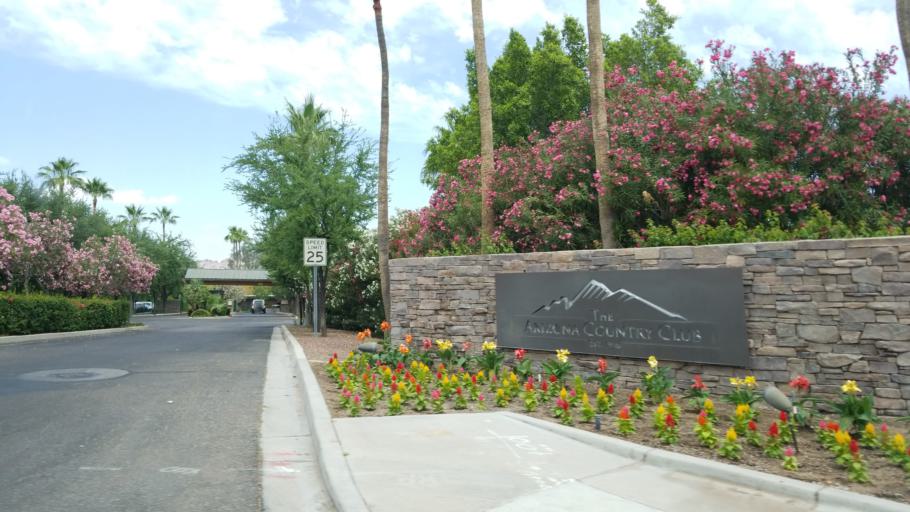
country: US
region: Arizona
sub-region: Maricopa County
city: Paradise Valley
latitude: 33.4801
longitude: -111.9574
